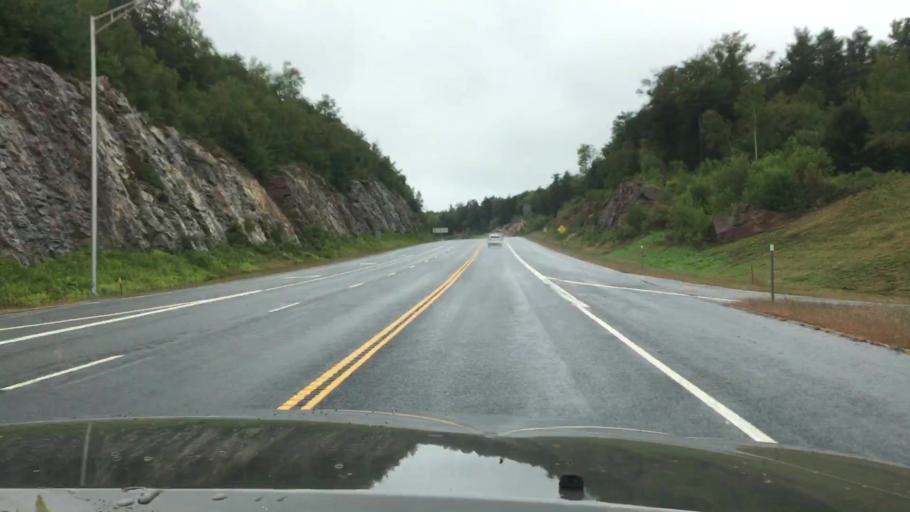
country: US
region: New Hampshire
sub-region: Cheshire County
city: Harrisville
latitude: 43.0063
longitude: -72.1609
